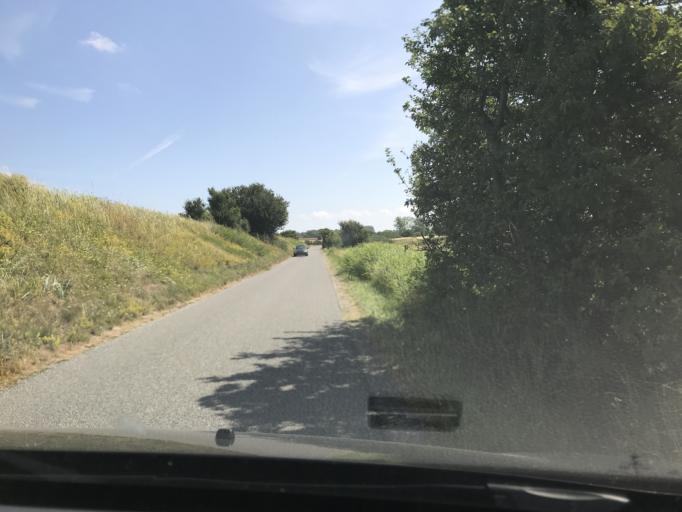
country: DK
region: South Denmark
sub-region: AEro Kommune
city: AEroskobing
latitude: 54.8842
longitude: 10.3776
